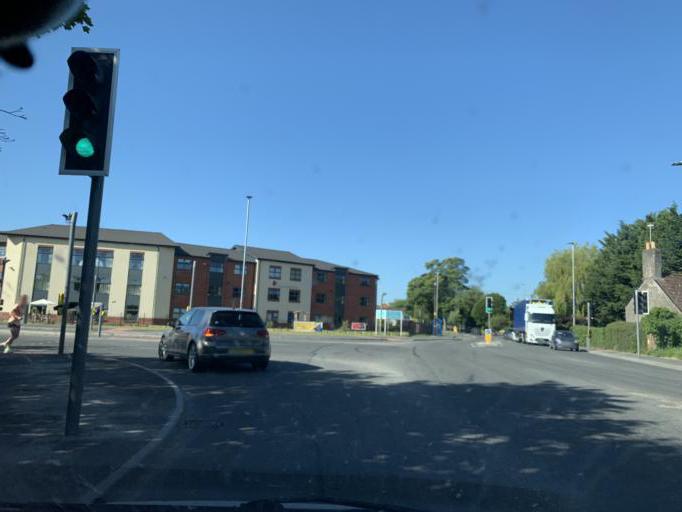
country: GB
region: England
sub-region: Wiltshire
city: Devizes
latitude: 51.3610
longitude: -1.9759
